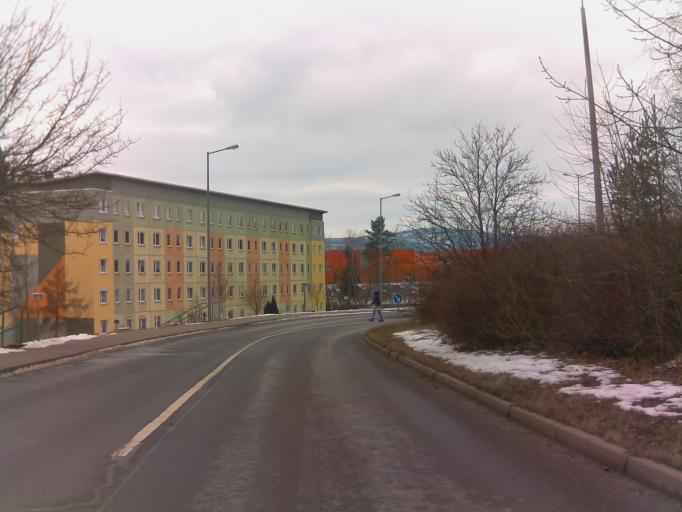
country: DE
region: Thuringia
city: Neuhaus
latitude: 50.6915
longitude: 10.9525
